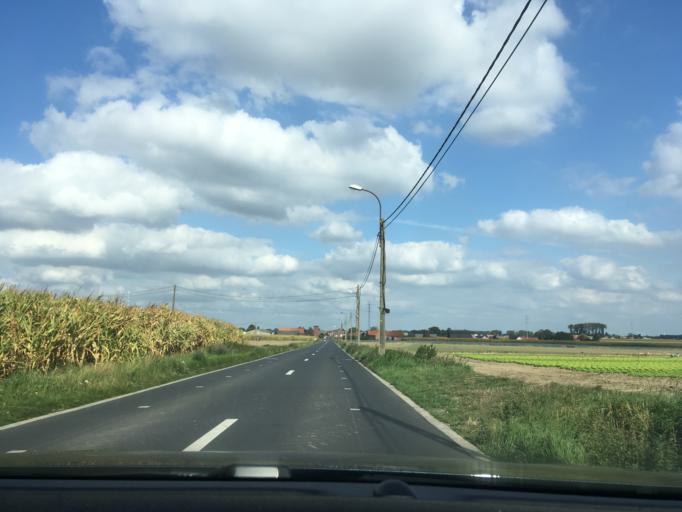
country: BE
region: Flanders
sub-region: Provincie West-Vlaanderen
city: Moorslede
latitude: 50.9166
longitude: 3.0321
